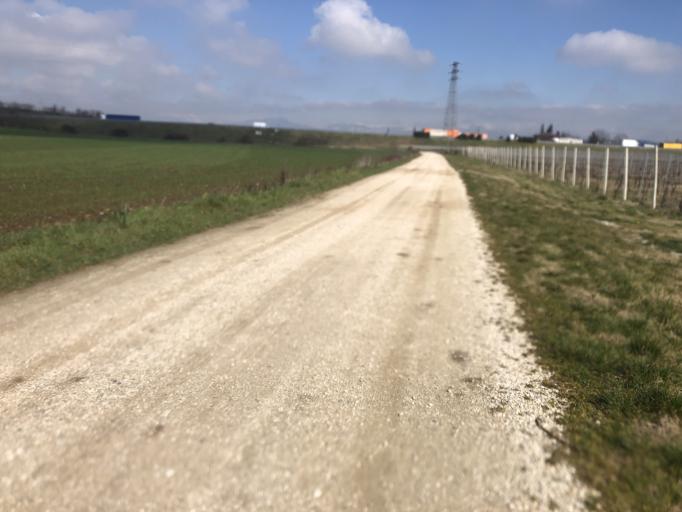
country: IT
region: Veneto
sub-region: Provincia di Verona
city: San Giorgio in Salici
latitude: 45.4157
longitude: 10.7946
